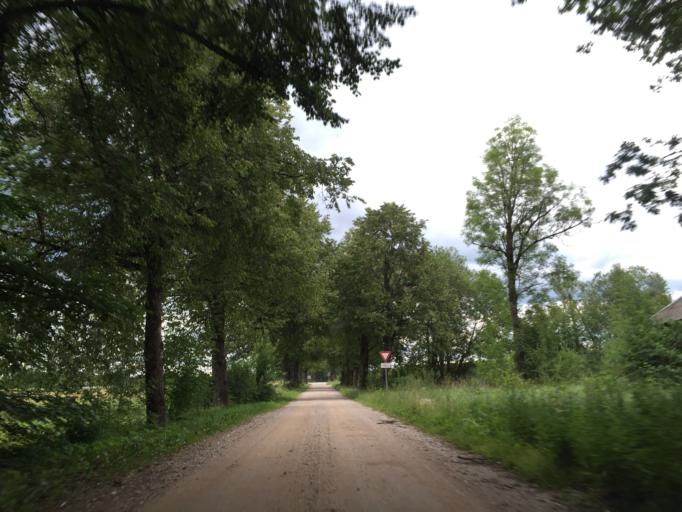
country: LV
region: Malpils
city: Malpils
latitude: 56.9229
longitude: 25.0061
